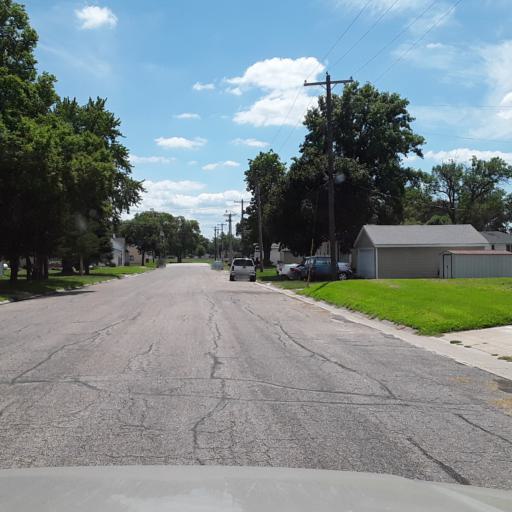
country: US
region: Nebraska
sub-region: Platte County
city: Columbus
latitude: 41.3914
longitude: -97.4947
